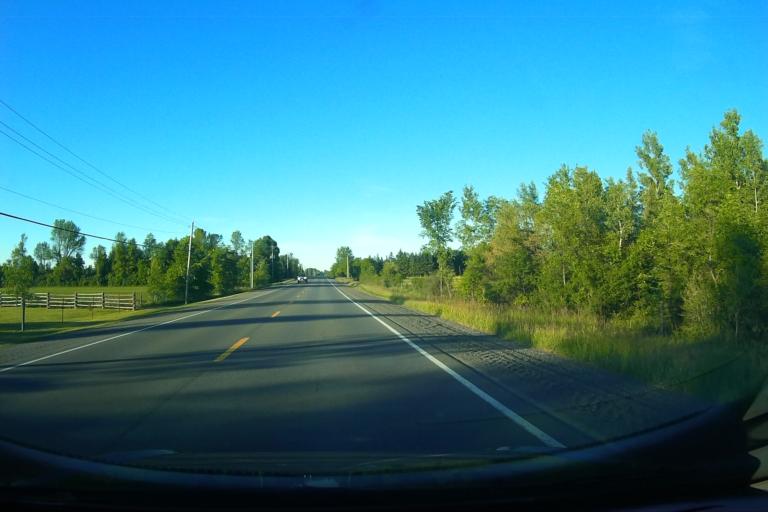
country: CA
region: Ontario
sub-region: Lanark County
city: Smiths Falls
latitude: 44.9685
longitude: -75.7533
